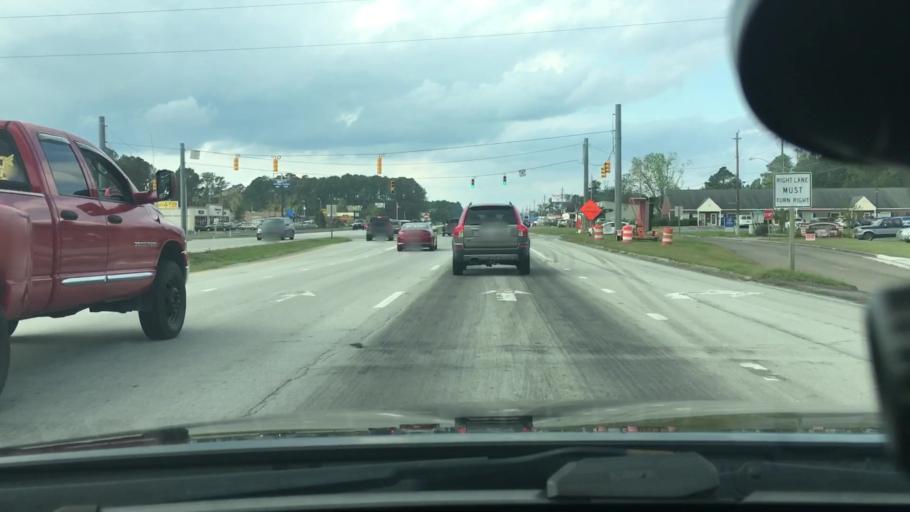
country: US
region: North Carolina
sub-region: Craven County
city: Havelock
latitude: 34.8960
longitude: -76.9270
